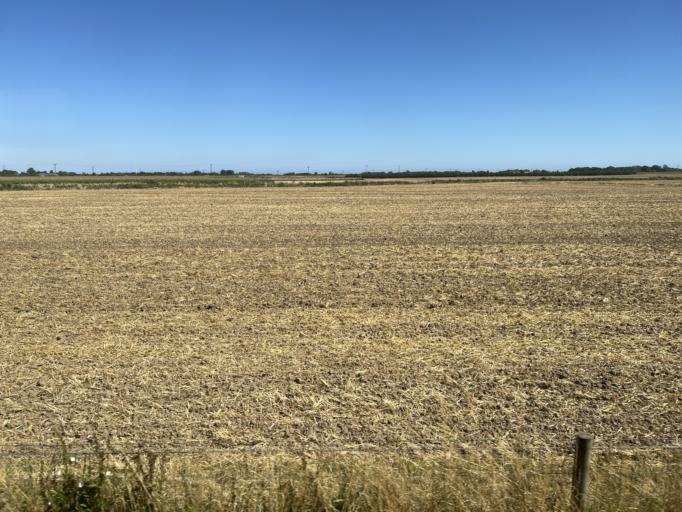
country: GB
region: England
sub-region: Lincolnshire
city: Wainfleet All Saints
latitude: 53.1128
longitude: 0.2181
